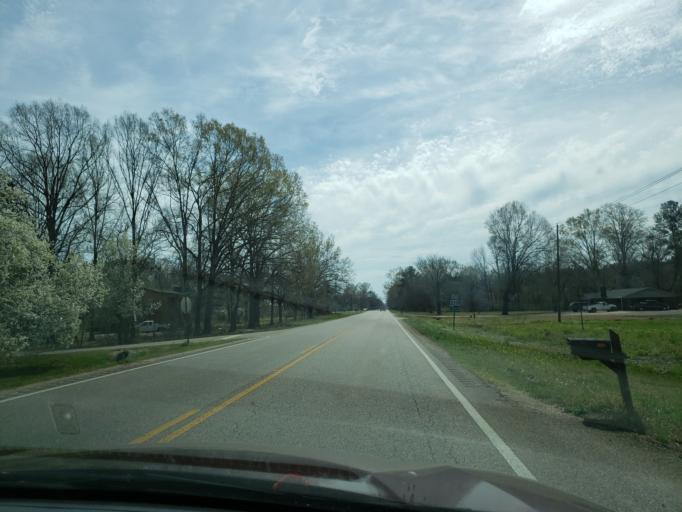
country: US
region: Alabama
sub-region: Dallas County
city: Selma
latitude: 32.4666
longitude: -87.0948
